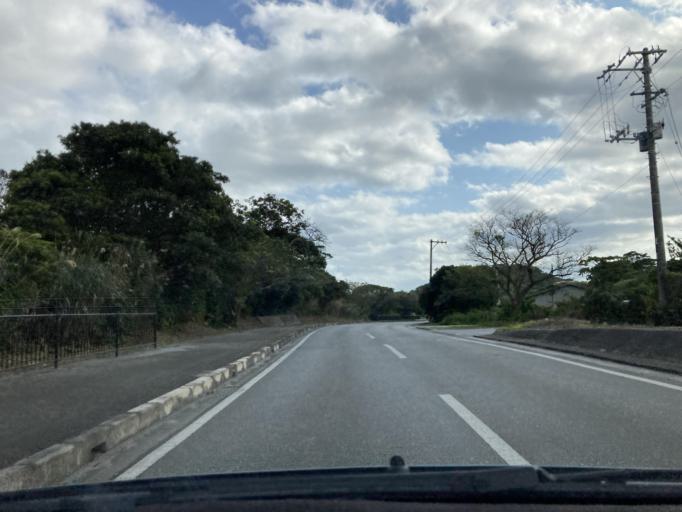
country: JP
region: Okinawa
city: Tomigusuku
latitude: 26.1789
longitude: 127.7607
